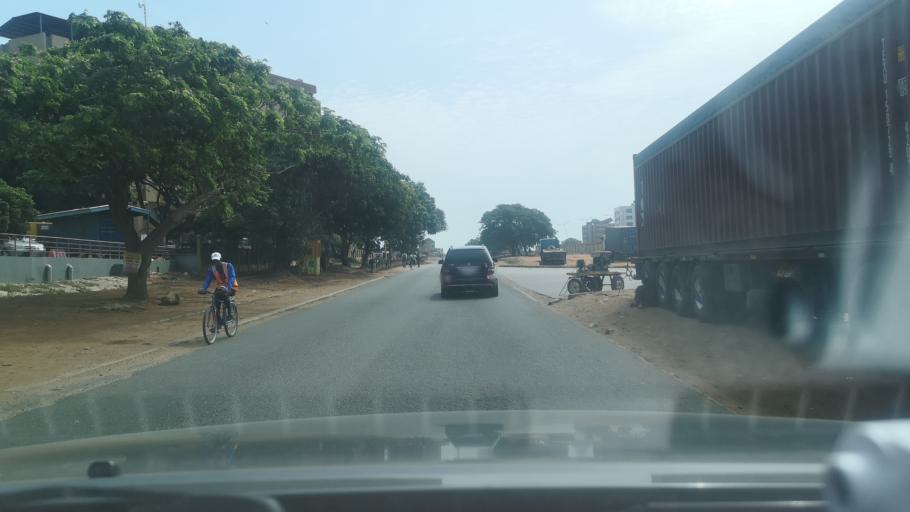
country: GH
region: Greater Accra
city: Tema
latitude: 5.6332
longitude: -0.0029
